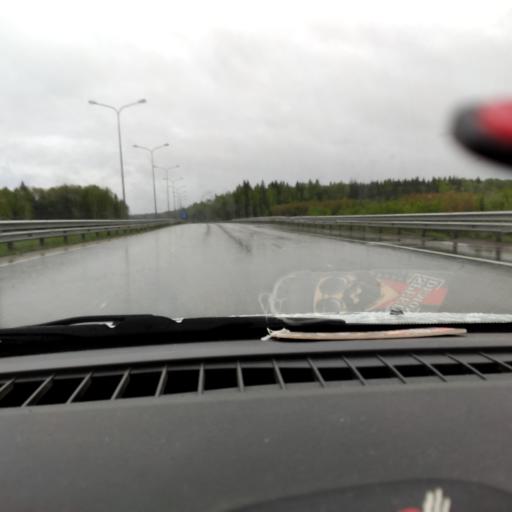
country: RU
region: Perm
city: Bershet'
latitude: 57.7062
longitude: 56.3686
